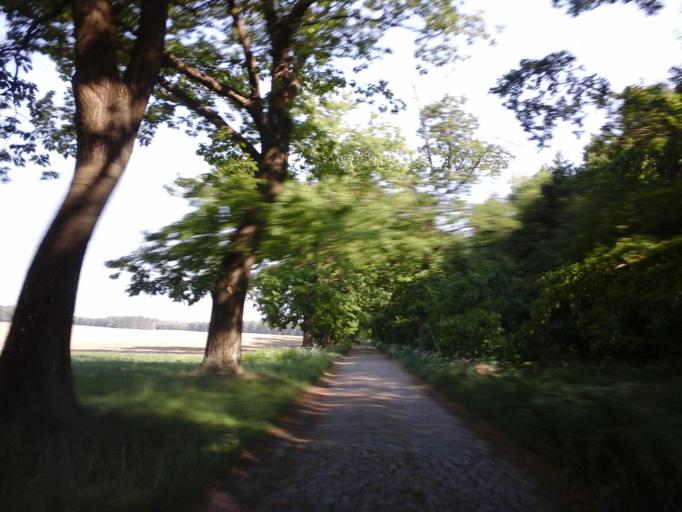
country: PL
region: West Pomeranian Voivodeship
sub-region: Powiat choszczenski
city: Recz
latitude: 53.2951
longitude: 15.5360
